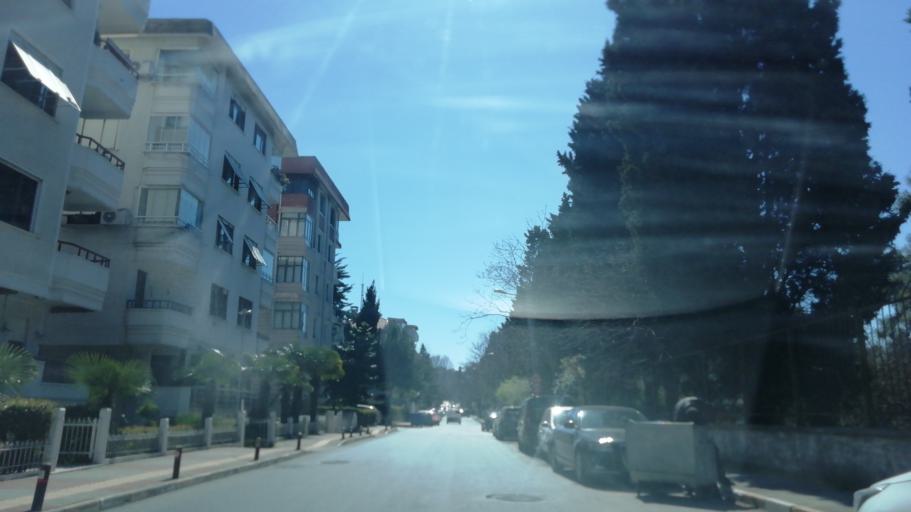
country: TR
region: Istanbul
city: Bahcelievler
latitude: 40.9863
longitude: 28.8663
